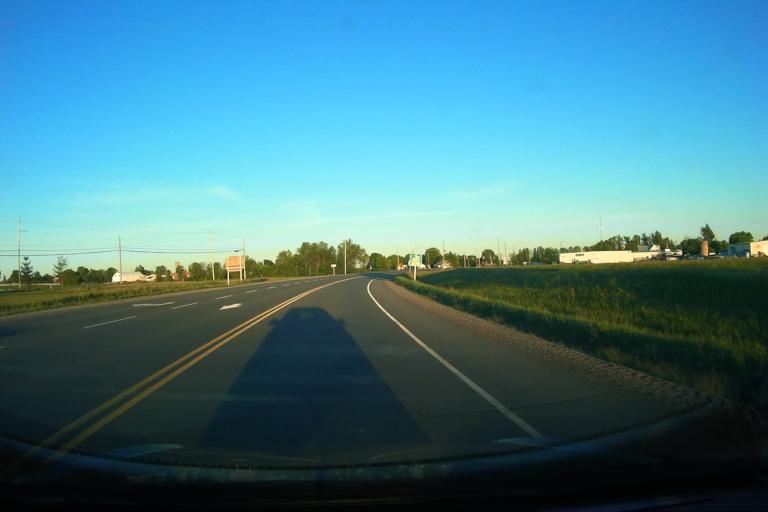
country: CA
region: Ontario
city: Casselman
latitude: 45.0734
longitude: -75.3401
